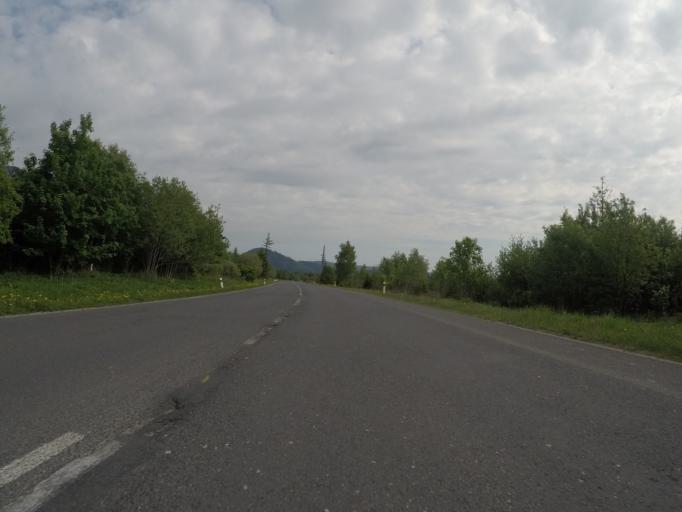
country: SK
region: Presovsky
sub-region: Okres Poprad
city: Nova Lesna
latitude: 49.1949
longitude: 20.3016
